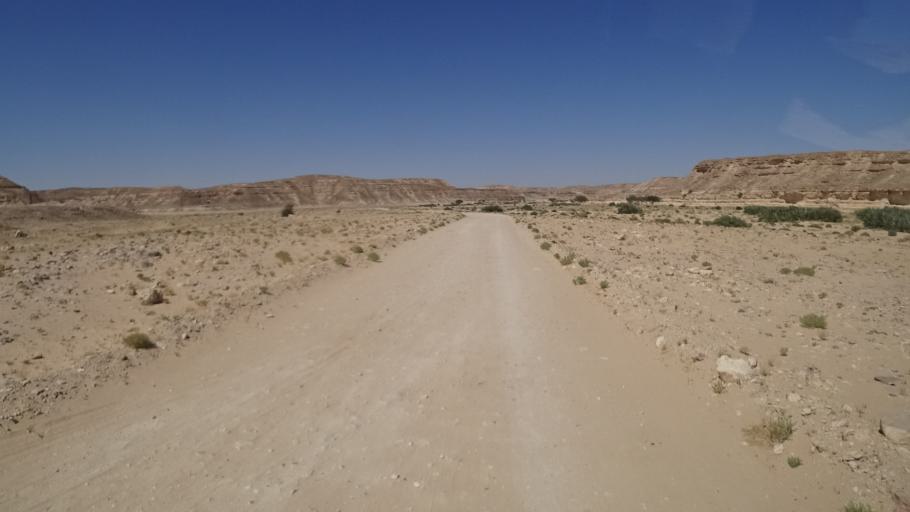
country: OM
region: Zufar
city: Salalah
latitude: 17.5015
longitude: 53.3650
